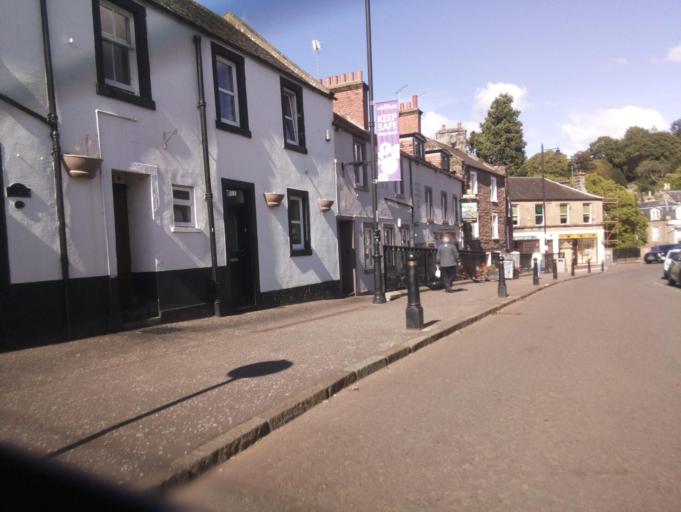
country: GB
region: Scotland
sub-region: Stirling
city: Dunblane
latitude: 56.1858
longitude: -3.9650
